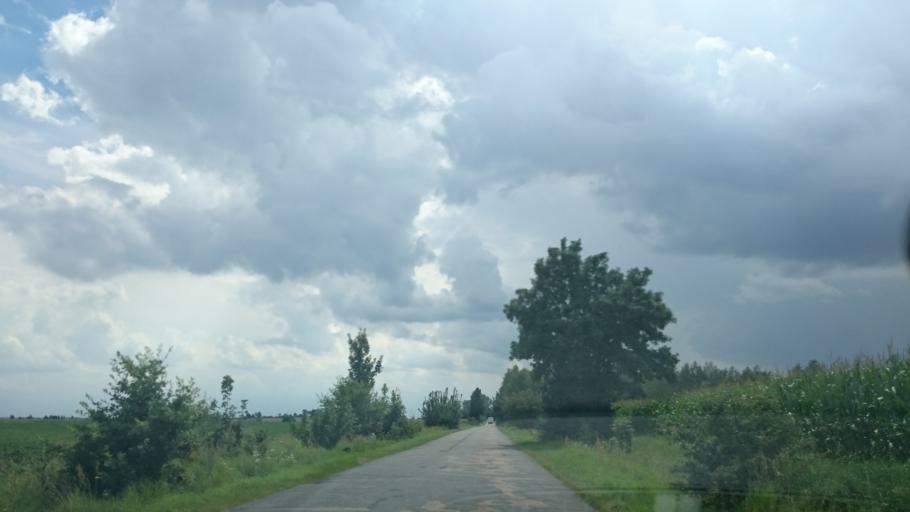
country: PL
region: Pomeranian Voivodeship
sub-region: Powiat chojnicki
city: Chojnice
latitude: 53.6902
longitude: 17.6780
